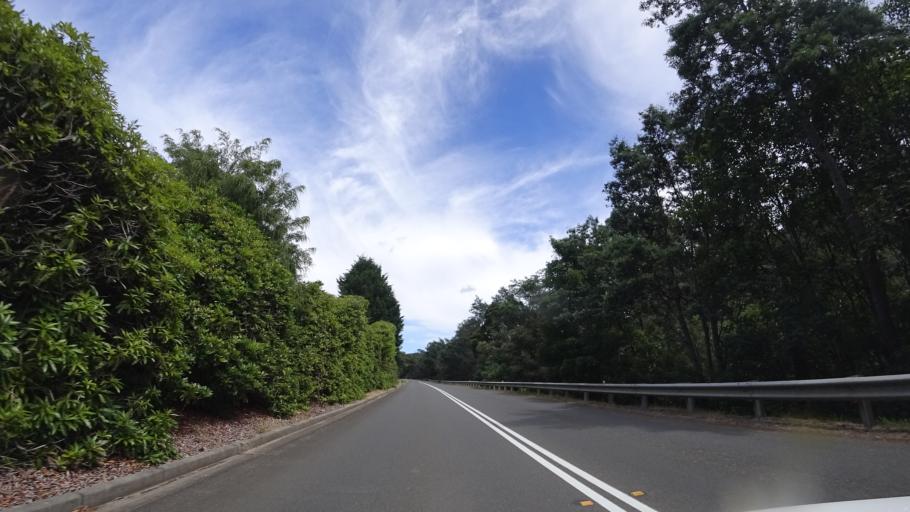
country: AU
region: Tasmania
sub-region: Dorset
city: Scottsdale
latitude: -41.1414
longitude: 147.7933
